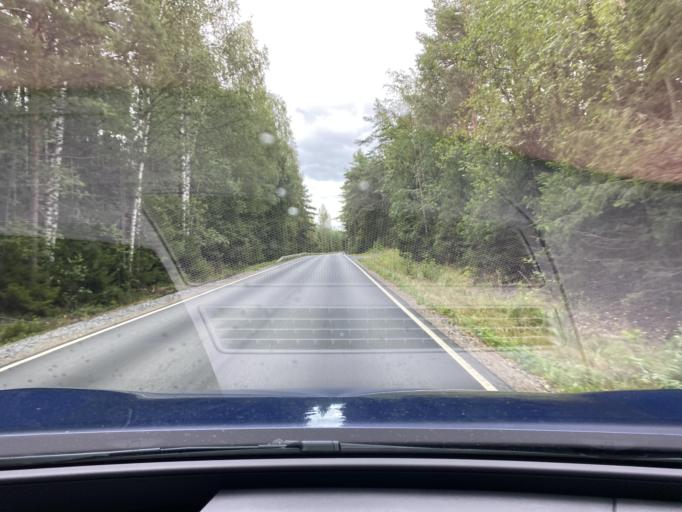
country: FI
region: Pirkanmaa
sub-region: Lounais-Pirkanmaa
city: Vammala
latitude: 61.2979
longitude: 22.9910
